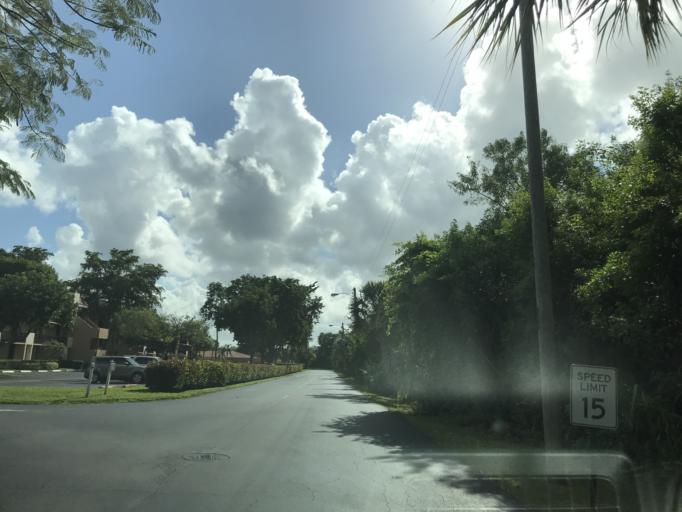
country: US
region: Florida
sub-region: Broward County
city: Margate
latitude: 26.2622
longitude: -80.1976
